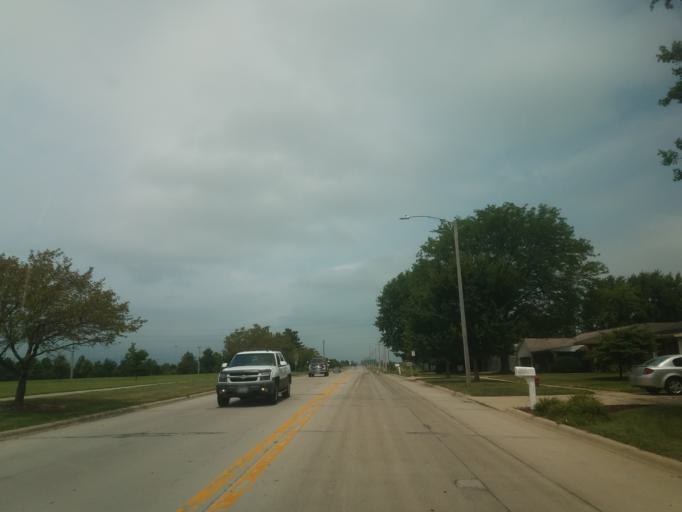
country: US
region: Illinois
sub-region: McLean County
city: Normal
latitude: 40.5158
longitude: -89.0212
